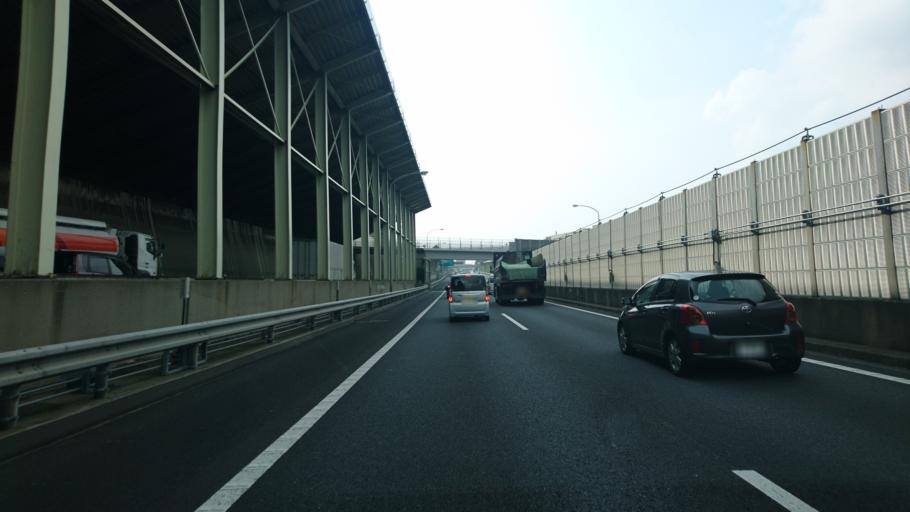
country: JP
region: Chiba
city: Chiba
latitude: 35.6382
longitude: 140.1187
